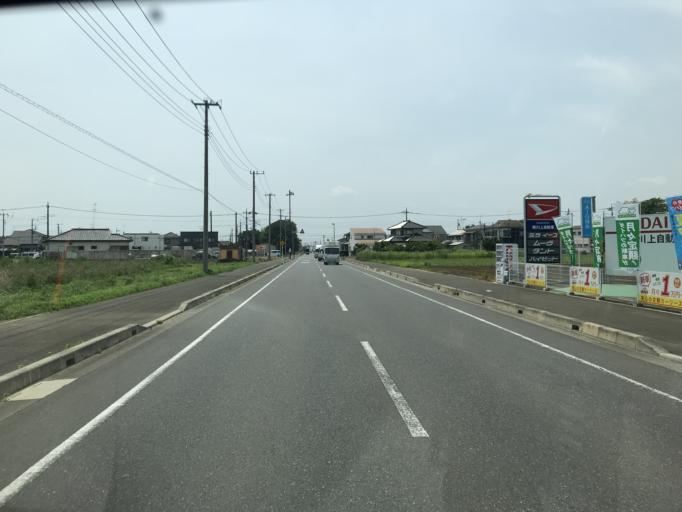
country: JP
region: Ibaraki
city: Sakai
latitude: 36.0387
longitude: 139.8275
